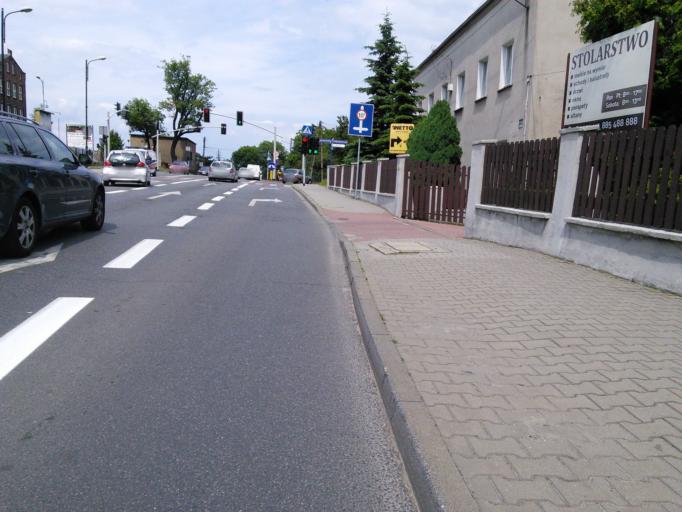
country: PL
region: Silesian Voivodeship
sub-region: Piekary Slaskie
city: Piekary Slaskie
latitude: 50.3905
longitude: 18.9456
